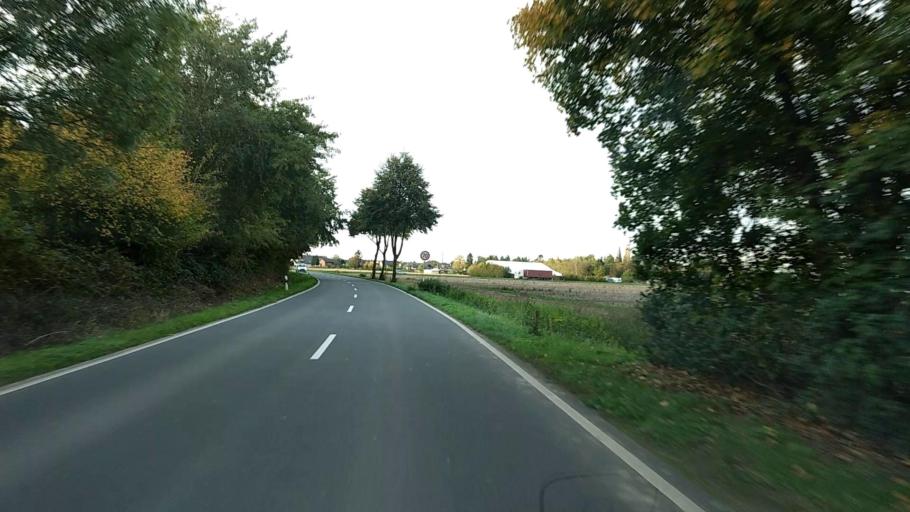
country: DE
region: North Rhine-Westphalia
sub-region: Regierungsbezirk Koln
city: Bergheim
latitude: 50.9072
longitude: 6.6394
